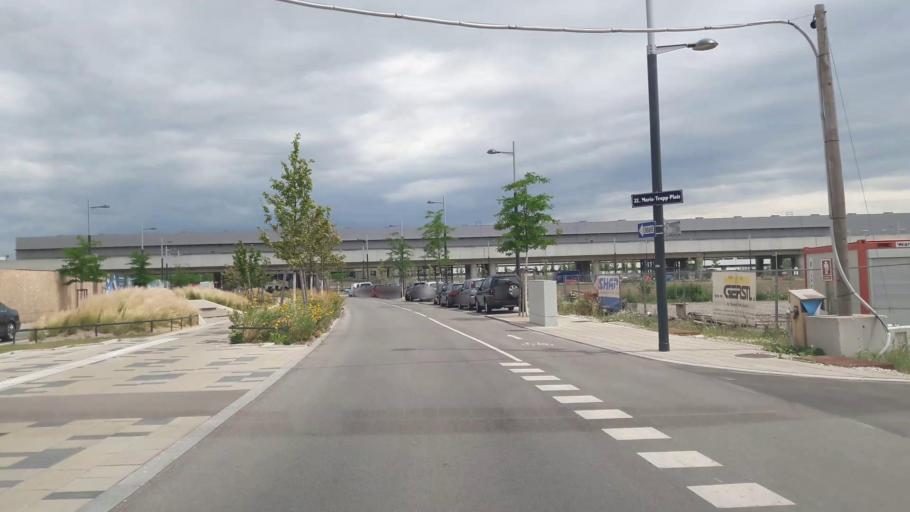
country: AT
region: Lower Austria
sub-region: Politischer Bezirk Ganserndorf
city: Gross-Enzersdorf
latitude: 48.2238
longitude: 16.5052
